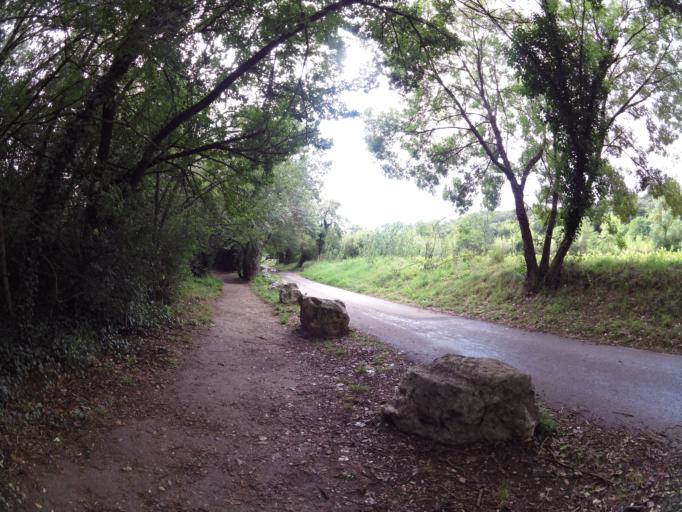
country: FR
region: Languedoc-Roussillon
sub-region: Departement du Gard
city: Sabran
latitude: 44.1923
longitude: 4.5235
